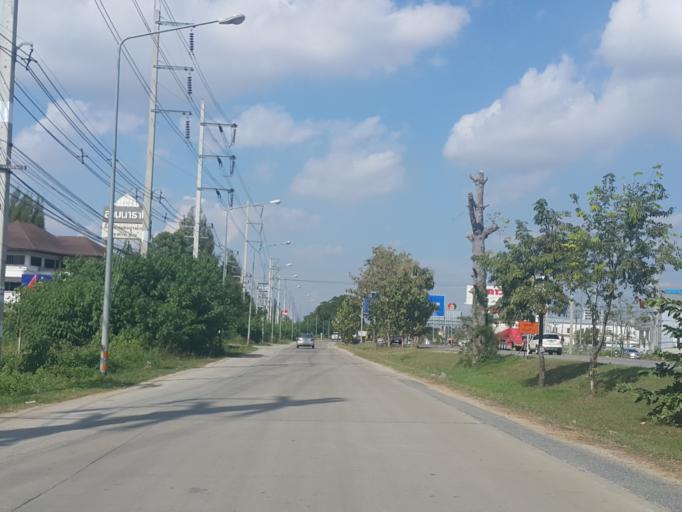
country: TH
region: Chiang Mai
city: Saraphi
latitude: 18.7400
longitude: 99.0358
